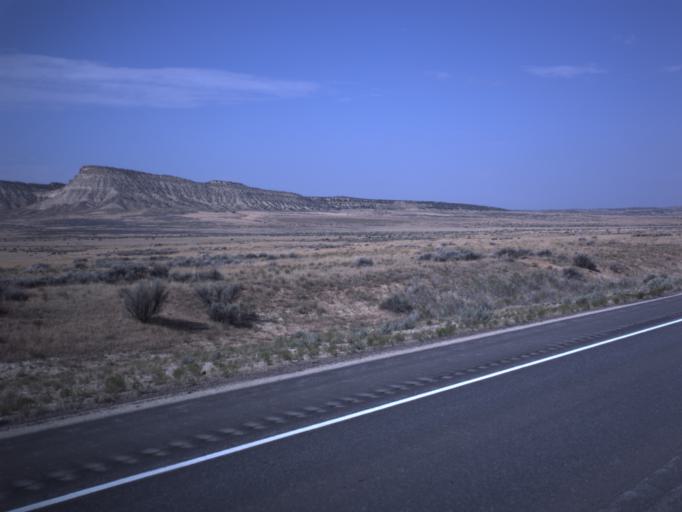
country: US
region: Colorado
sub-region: Rio Blanco County
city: Rangely
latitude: 40.2834
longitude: -109.1034
